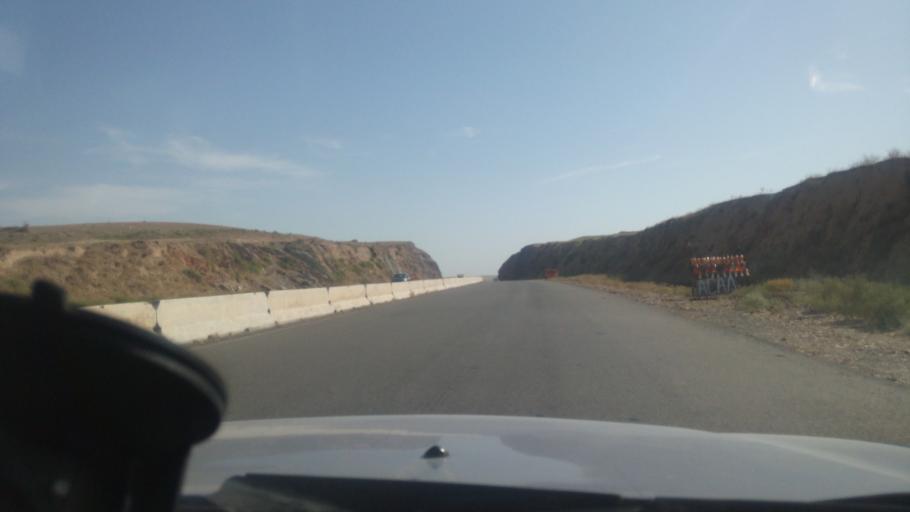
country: UZ
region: Jizzax
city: Jizzax
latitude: 40.0469
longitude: 67.6750
